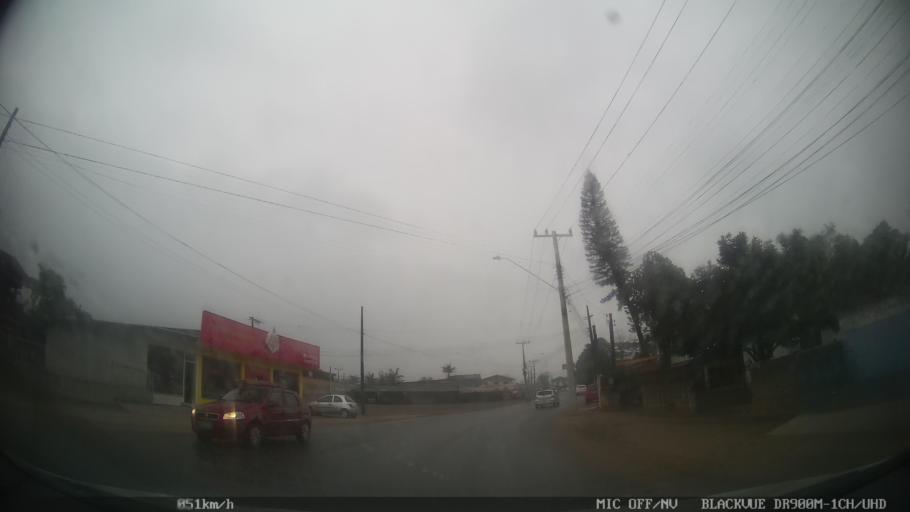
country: BR
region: Santa Catarina
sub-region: Joinville
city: Joinville
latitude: -26.2187
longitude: -48.8195
